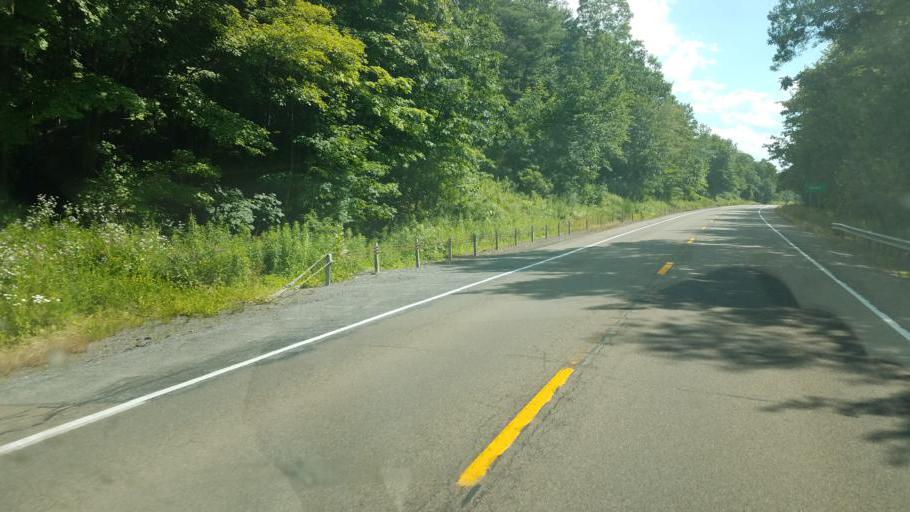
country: US
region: New York
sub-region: Steuben County
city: Sylvan Beach
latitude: 42.5009
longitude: -77.1102
